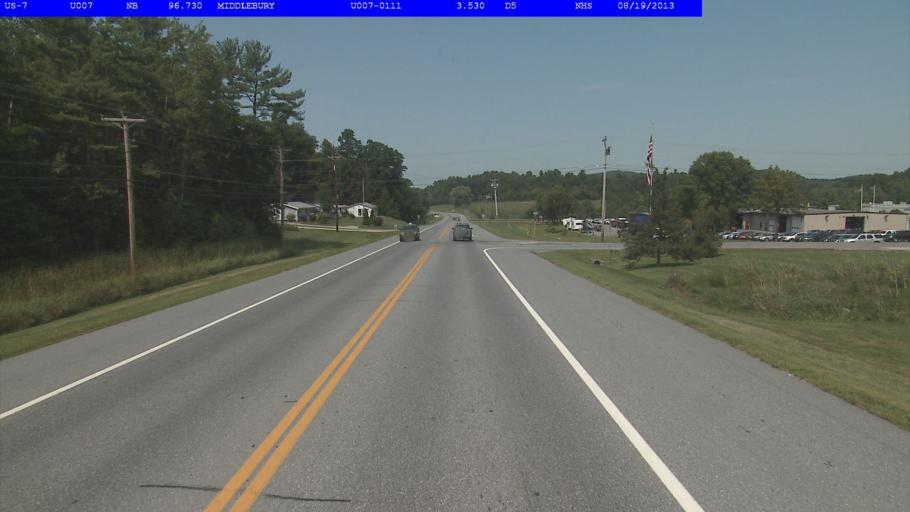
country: US
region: Vermont
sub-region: Addison County
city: Middlebury (village)
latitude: 43.9984
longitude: -73.1469
